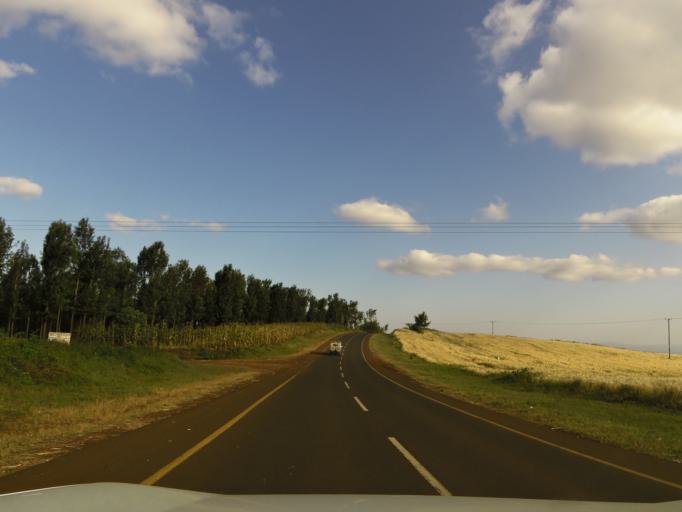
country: TZ
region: Arusha
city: Kiratu
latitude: -3.3247
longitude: 35.6010
